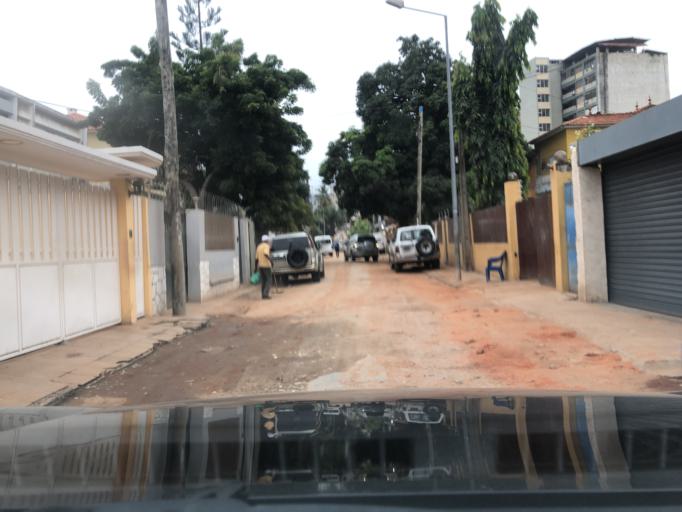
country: AO
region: Luanda
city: Luanda
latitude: -8.8202
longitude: 13.2517
